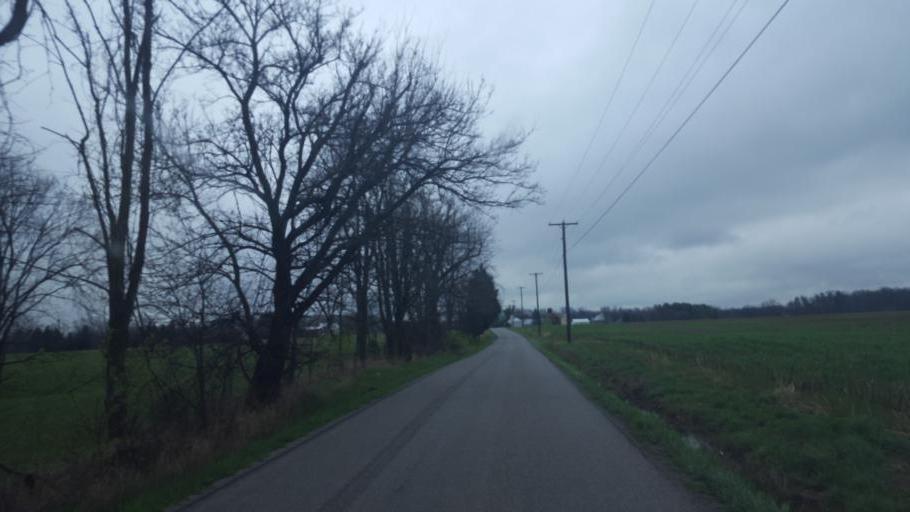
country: US
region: Ohio
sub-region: Morrow County
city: Cardington
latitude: 40.5043
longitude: -82.8722
